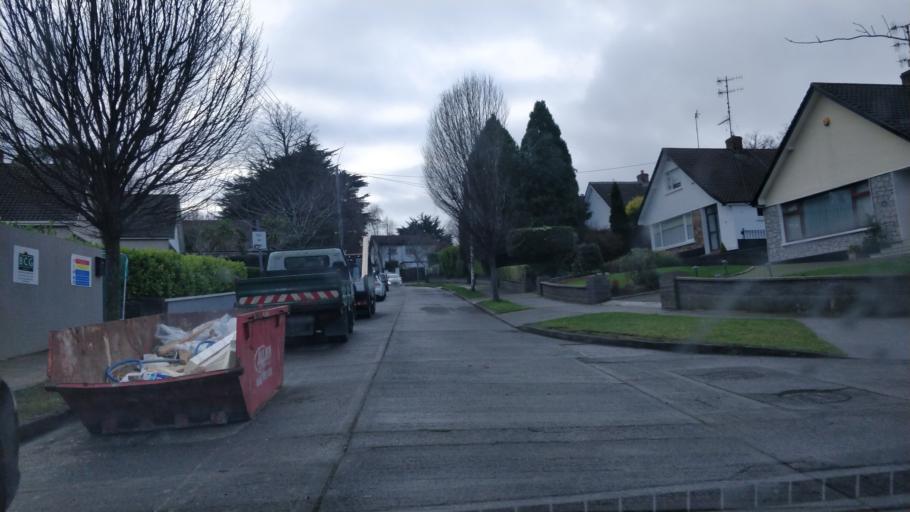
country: IE
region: Leinster
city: Foxrock
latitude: 53.2766
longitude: -6.1775
